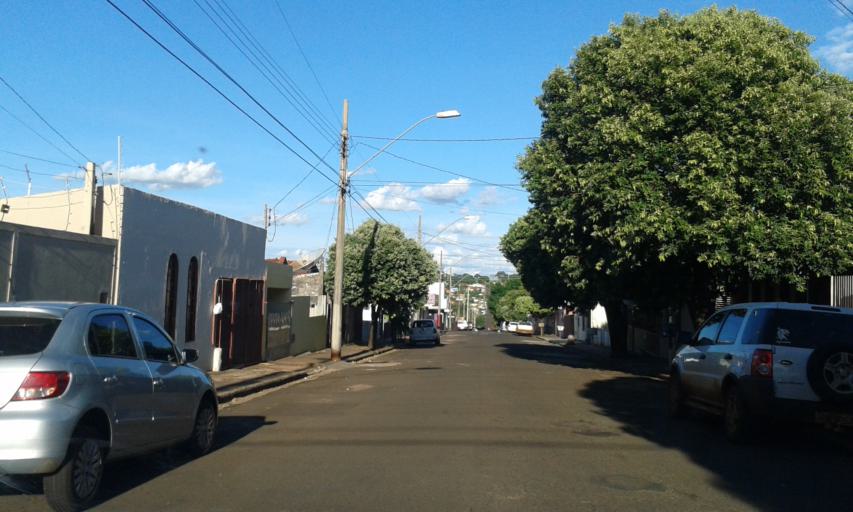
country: BR
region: Minas Gerais
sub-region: Ituiutaba
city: Ituiutaba
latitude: -18.9783
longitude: -49.4545
